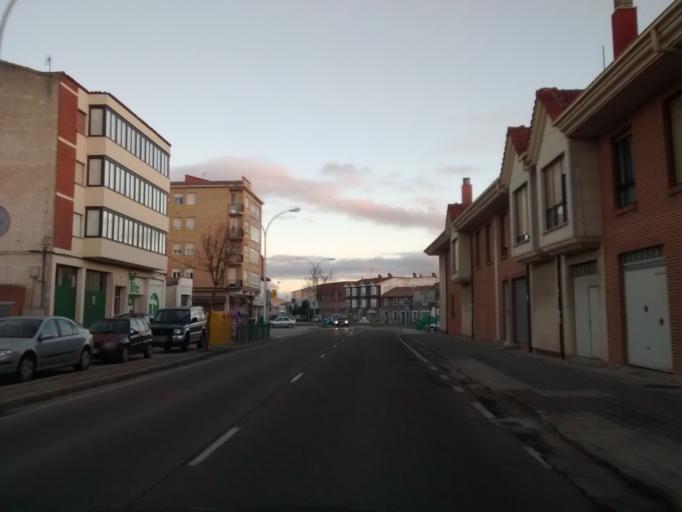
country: ES
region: Castille and Leon
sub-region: Provincia de Palencia
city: Aguilar de Campoo
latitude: 42.7943
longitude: -4.2581
